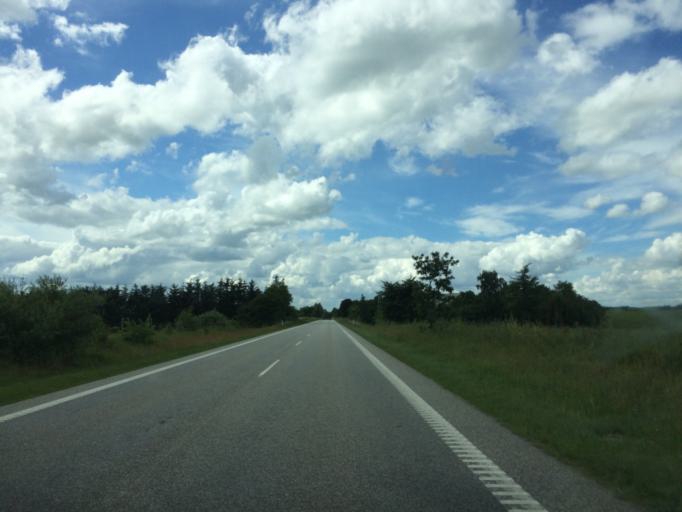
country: DK
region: North Denmark
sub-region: Vesthimmerland Kommune
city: Alestrup
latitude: 56.6220
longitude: 9.5639
